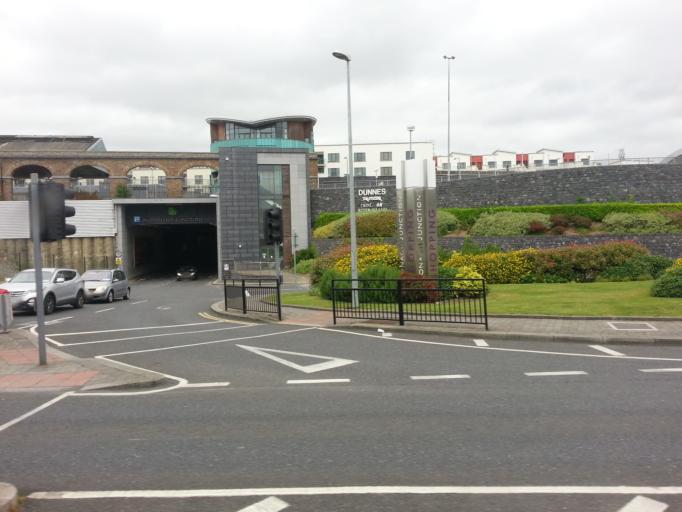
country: IE
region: Leinster
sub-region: Kilkenny
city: Kilkenny
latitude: 52.6541
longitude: -7.2449
